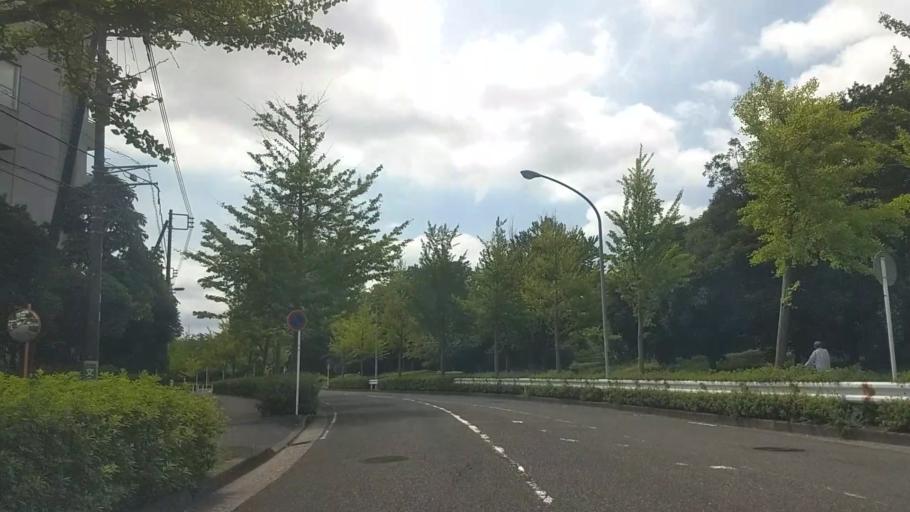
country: JP
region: Kanagawa
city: Yokosuka
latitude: 35.3565
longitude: 139.6390
